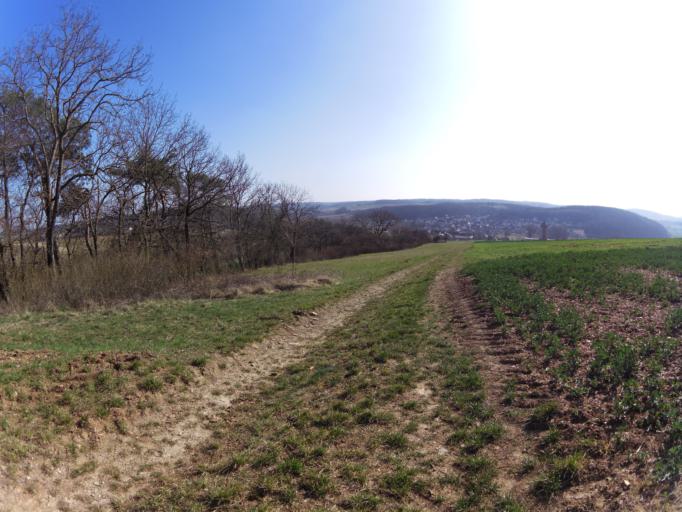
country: DE
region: Bavaria
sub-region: Regierungsbezirk Unterfranken
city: Greussenheim
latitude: 49.8049
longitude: 9.7605
